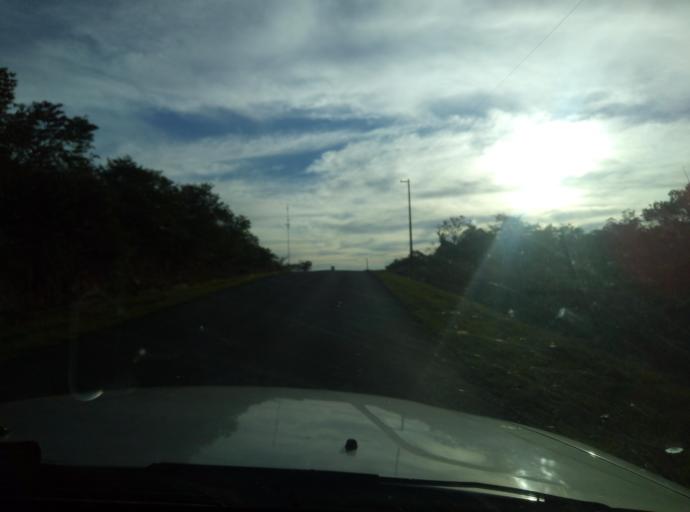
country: PY
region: Caaguazu
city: Carayao
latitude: -25.1536
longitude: -56.3222
